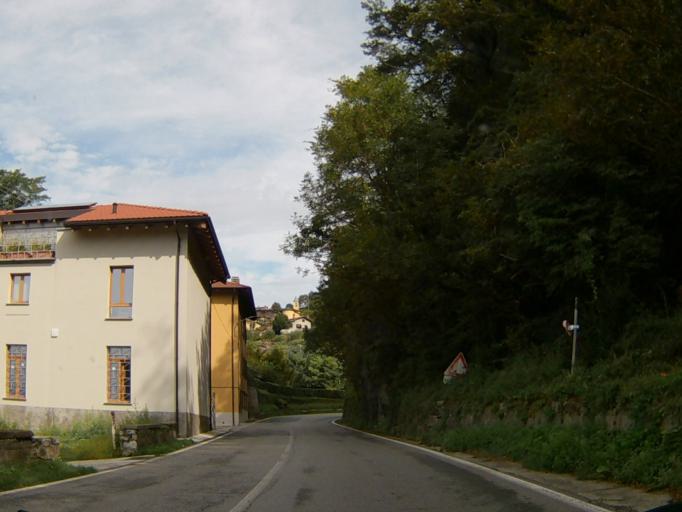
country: IT
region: Lombardy
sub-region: Provincia di Lecco
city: Dorio
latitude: 46.1123
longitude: 9.3169
